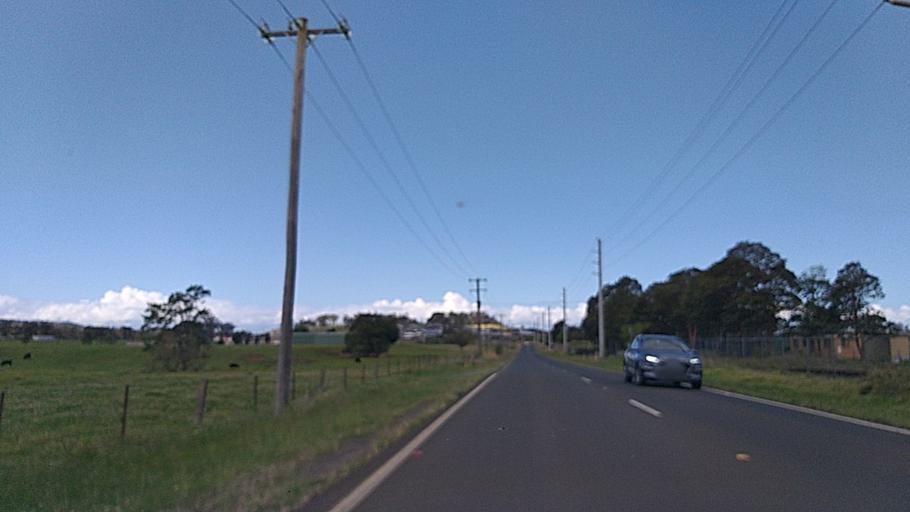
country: AU
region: New South Wales
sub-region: Wollongong
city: Dapto
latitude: -34.4792
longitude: 150.7742
